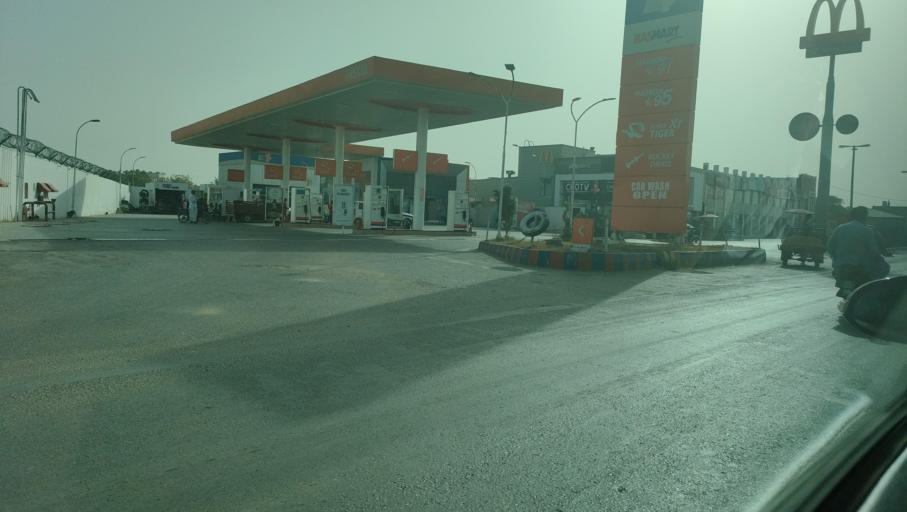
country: PK
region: Sindh
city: Malir Cantonment
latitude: 24.9226
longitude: 67.1837
